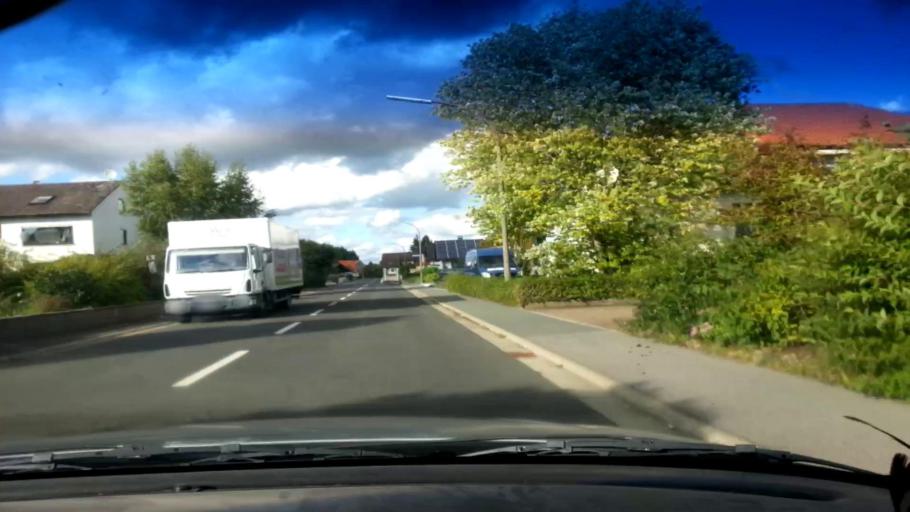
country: DE
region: Bavaria
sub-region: Upper Franconia
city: Ebensfeld
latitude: 50.0649
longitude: 10.9521
